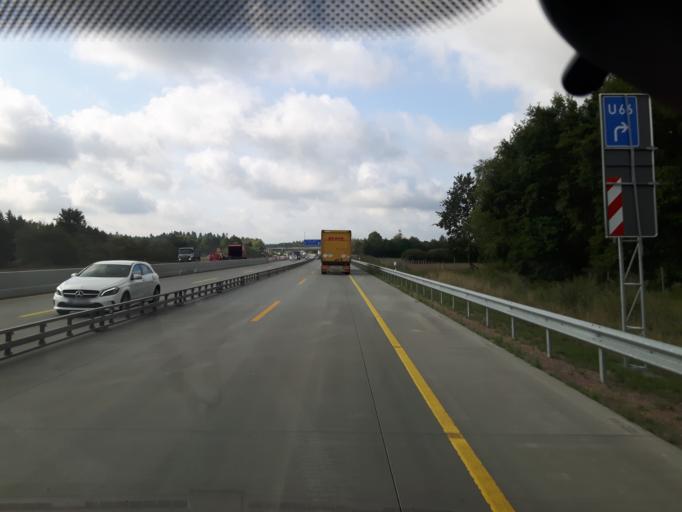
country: DE
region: Schleswig-Holstein
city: Bimohlen
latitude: 53.9127
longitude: 9.9367
